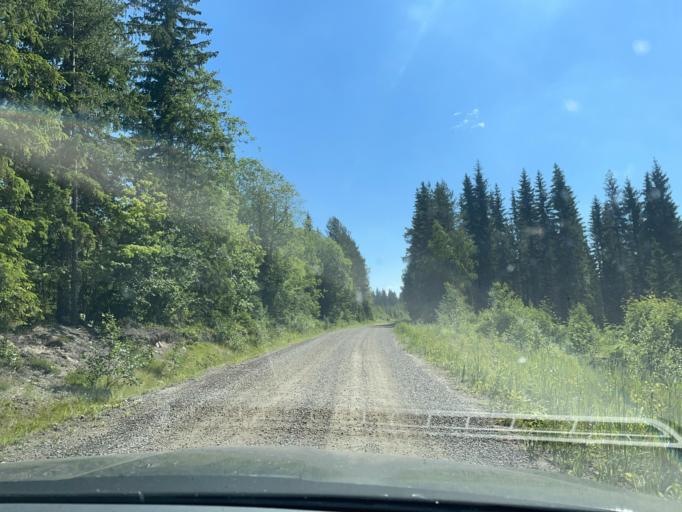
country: FI
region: Central Finland
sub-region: Saarijaervi-Viitasaari
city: Viitasaari
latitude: 63.2374
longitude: 25.9512
